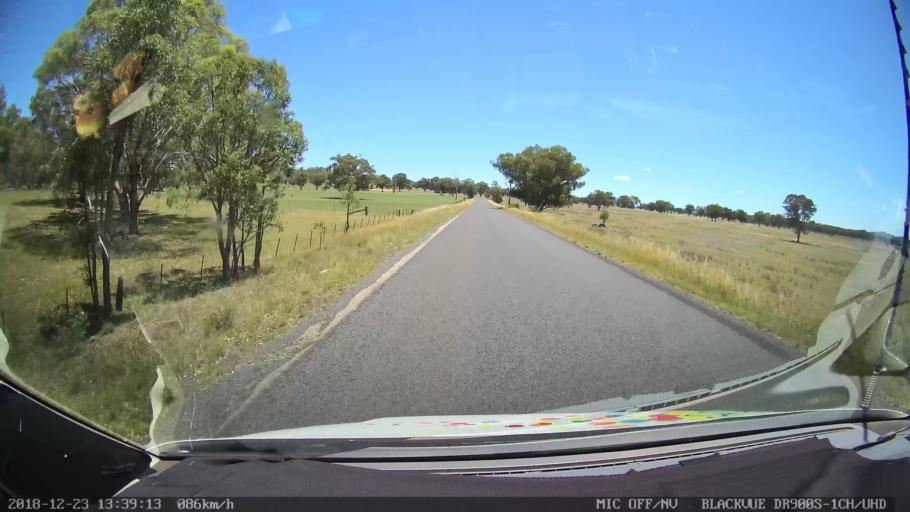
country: AU
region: New South Wales
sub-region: Armidale Dumaresq
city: Armidale
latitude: -30.4562
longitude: 151.2043
